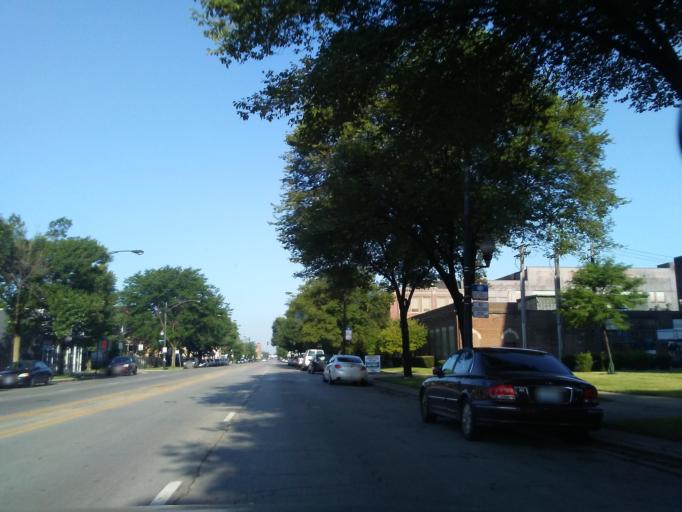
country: US
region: Illinois
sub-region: Cook County
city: Oak Park
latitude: 41.9245
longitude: -87.7295
